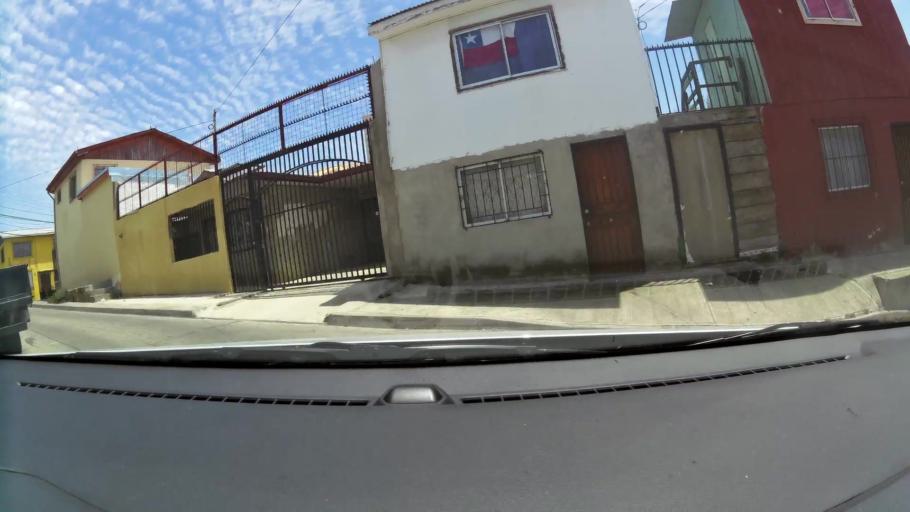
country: CL
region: Valparaiso
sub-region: Provincia de Valparaiso
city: Valparaiso
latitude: -33.0459
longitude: -71.5943
